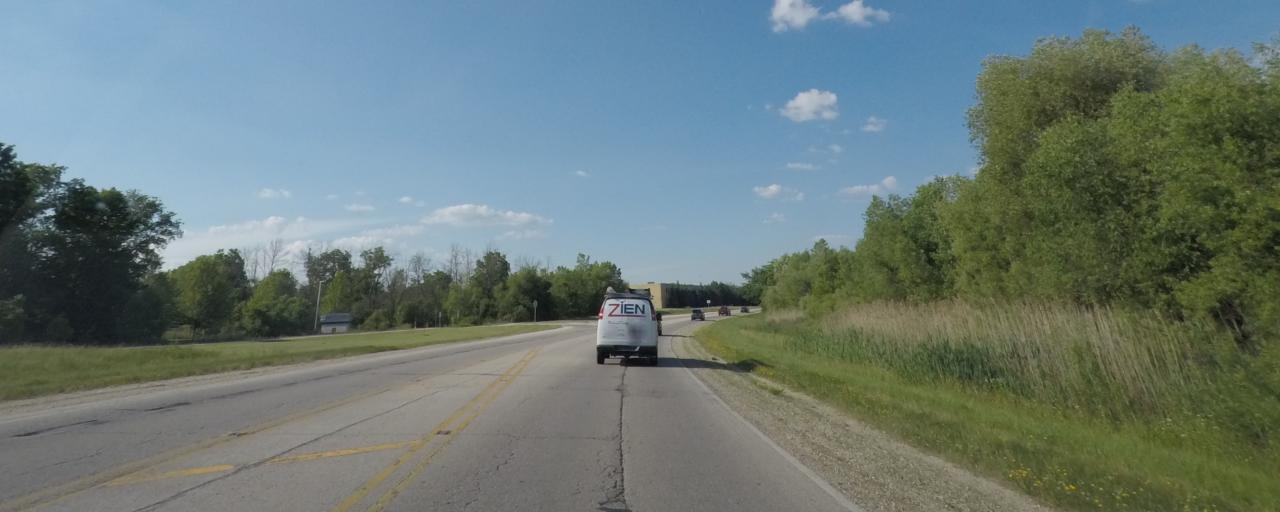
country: US
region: Wisconsin
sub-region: Waukesha County
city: Muskego
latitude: 42.9359
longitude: -88.1133
